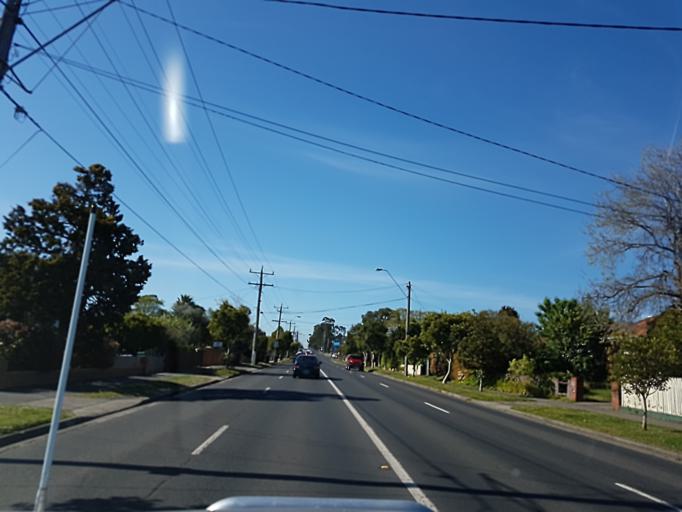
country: AU
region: Victoria
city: Clayton
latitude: -37.9166
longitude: 145.1213
